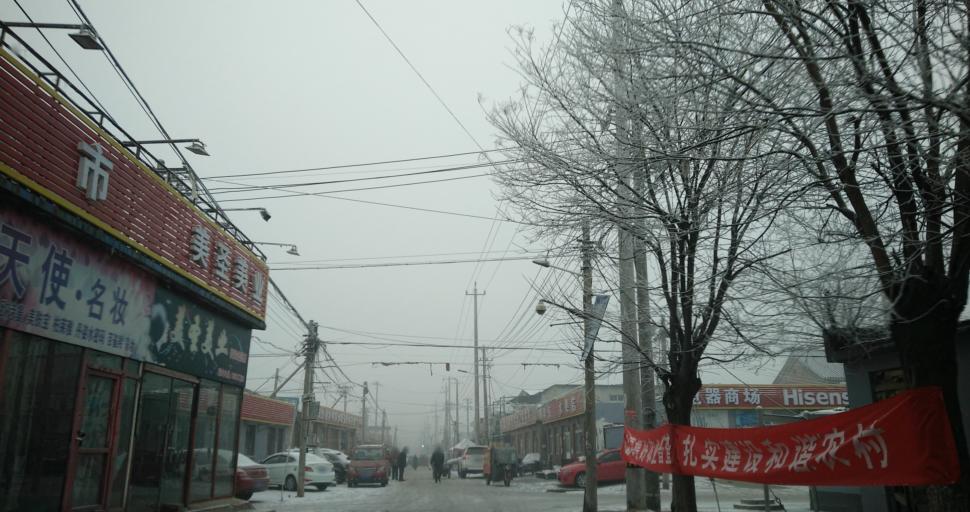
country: CN
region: Beijing
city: Yinghai
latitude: 39.7170
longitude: 116.4273
